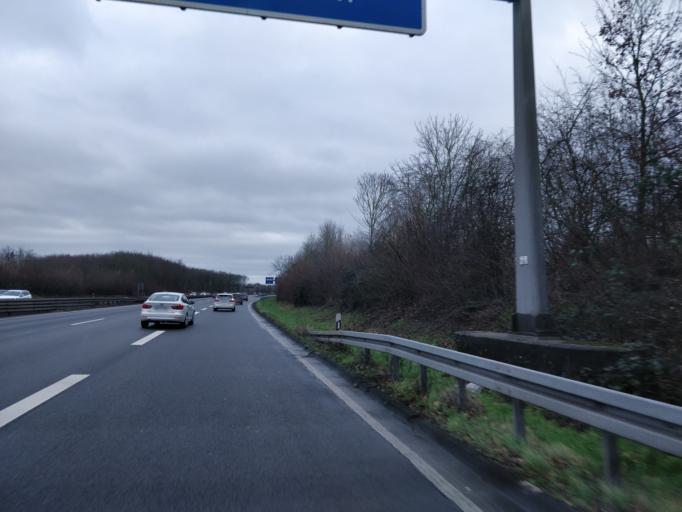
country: DE
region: North Rhine-Westphalia
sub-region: Regierungsbezirk Koln
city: Eil
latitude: 50.8905
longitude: 7.0921
